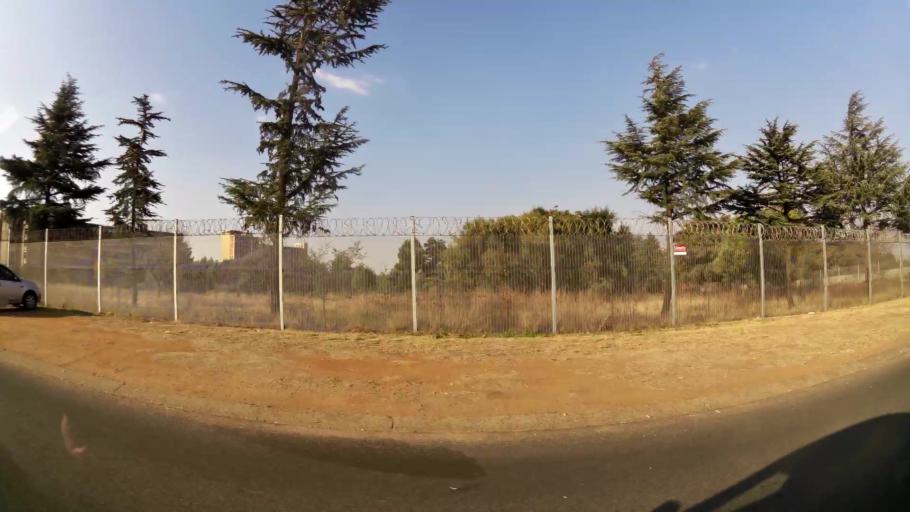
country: ZA
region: Gauteng
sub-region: City of Johannesburg Metropolitan Municipality
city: Modderfontein
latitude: -26.0747
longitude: 28.2151
